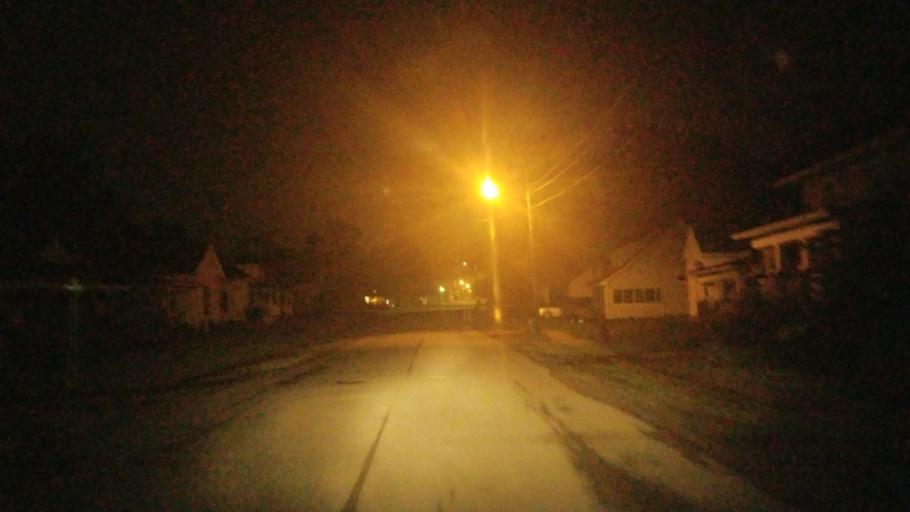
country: US
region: Missouri
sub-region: Pike County
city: Bowling Green
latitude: 39.3393
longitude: -91.1952
